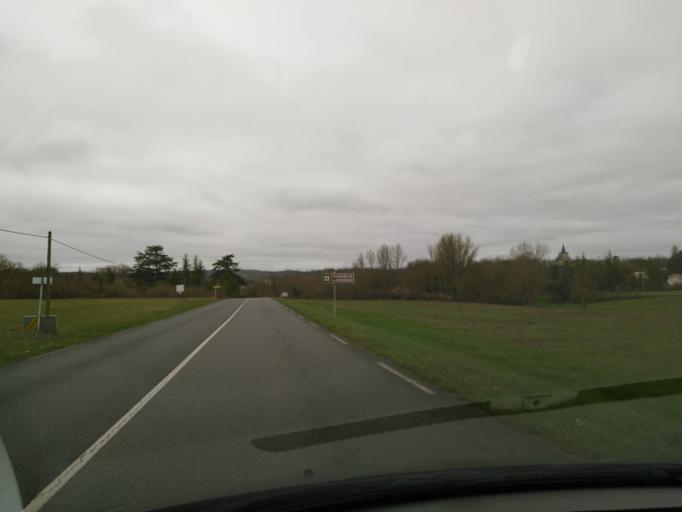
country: FR
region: Aquitaine
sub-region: Departement du Lot-et-Garonne
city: Castillonnes
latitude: 44.6971
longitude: 0.5661
